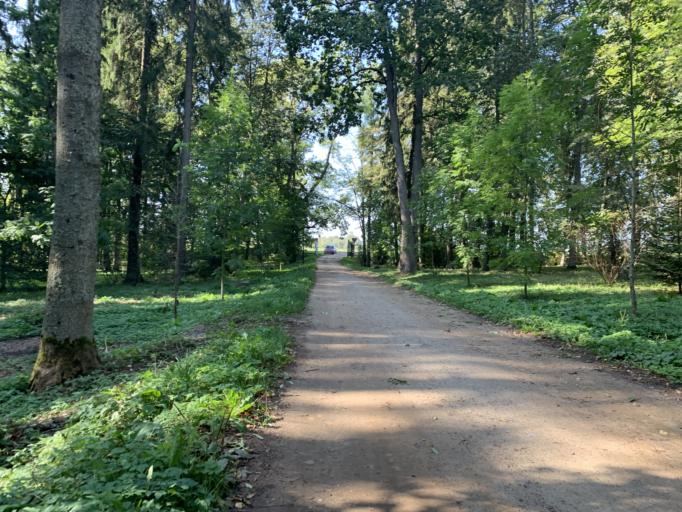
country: BY
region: Minsk
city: Rakaw
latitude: 53.8756
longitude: 26.9665
